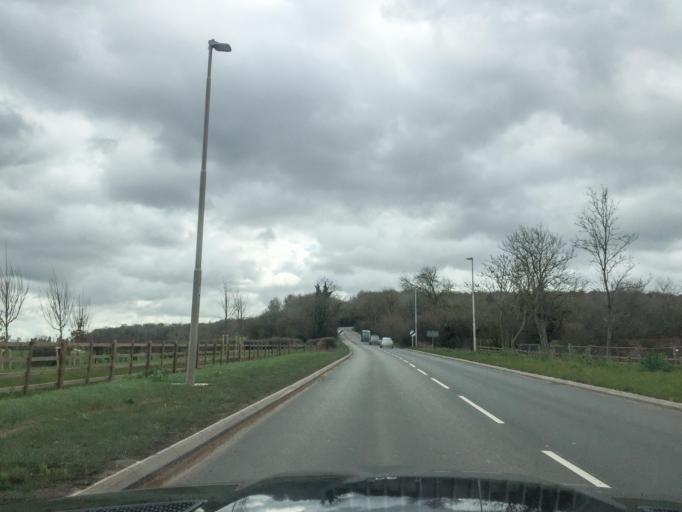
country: GB
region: England
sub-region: Warwickshire
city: Wellesbourne Mountford
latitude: 52.1841
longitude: -1.5974
